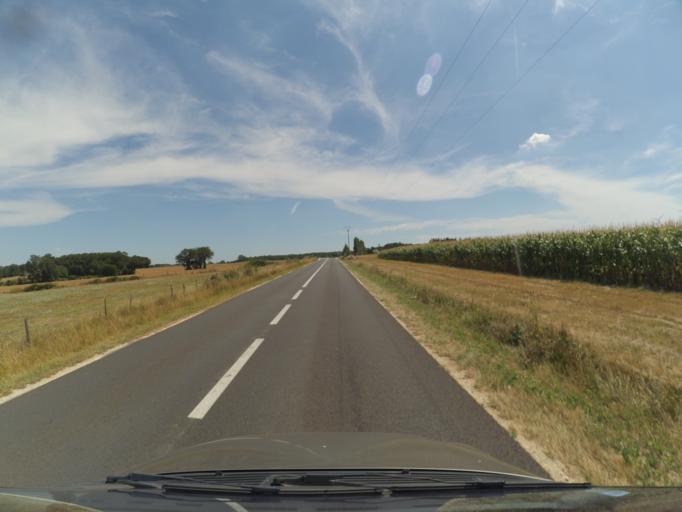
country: FR
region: Poitou-Charentes
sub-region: Departement de la Vienne
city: Saint-Maurice-la-Clouere
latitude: 46.3556
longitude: 0.4434
